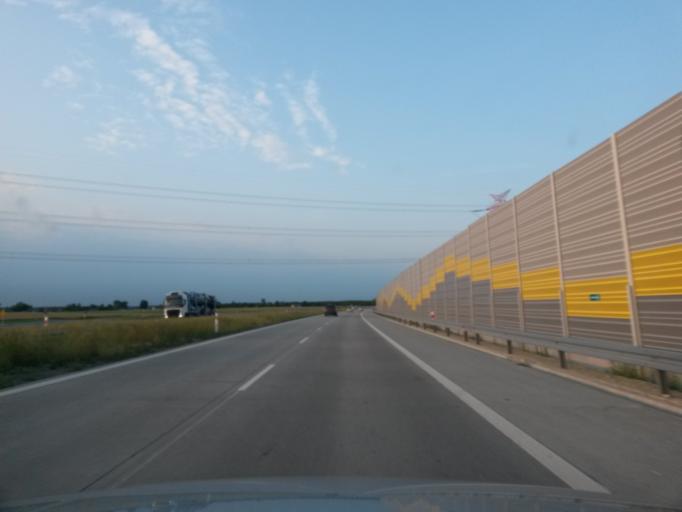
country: PL
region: Lodz Voivodeship
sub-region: Powiat sieradzki
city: Zloczew
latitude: 51.3838
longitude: 18.5563
